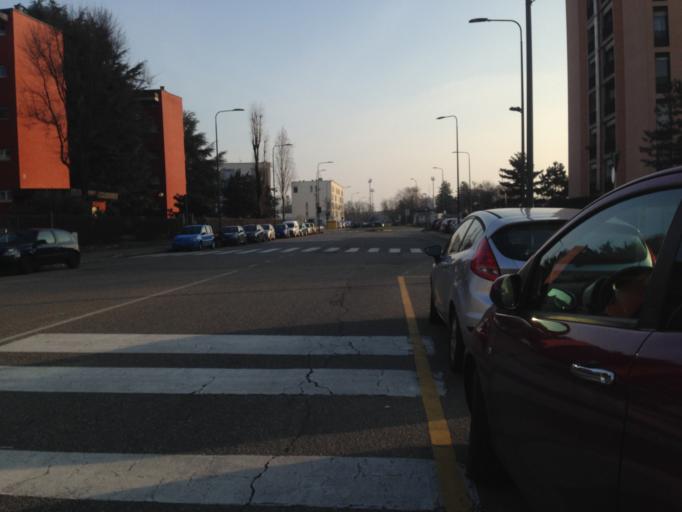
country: IT
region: Lombardy
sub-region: Citta metropolitana di Milano
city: Cesano Boscone
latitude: 45.4707
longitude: 9.1093
